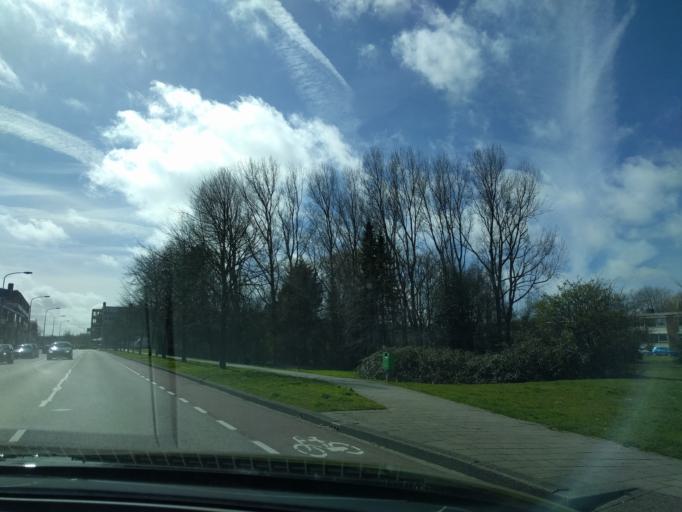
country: NL
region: South Holland
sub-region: Gemeente Katwijk
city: Katwijk aan den Rijn
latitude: 52.1985
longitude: 4.4137
